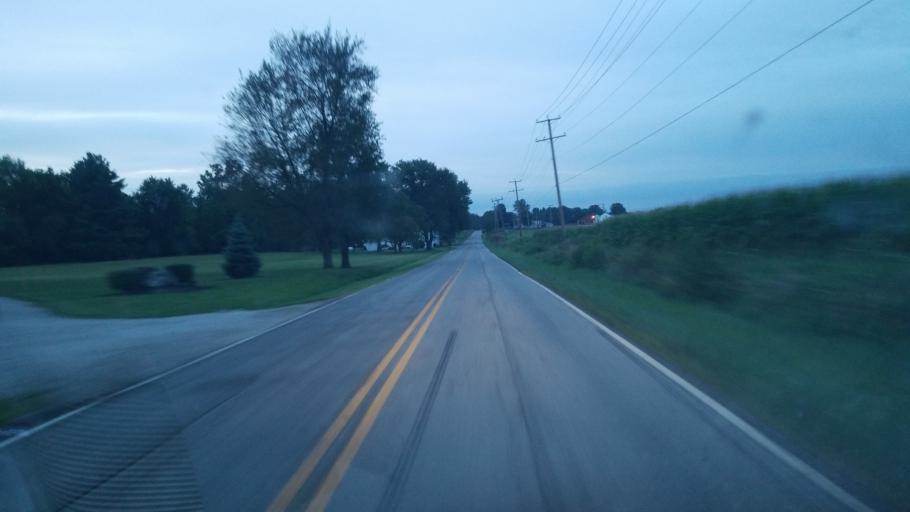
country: US
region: Ohio
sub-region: Knox County
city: Centerburg
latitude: 40.2535
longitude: -82.6936
